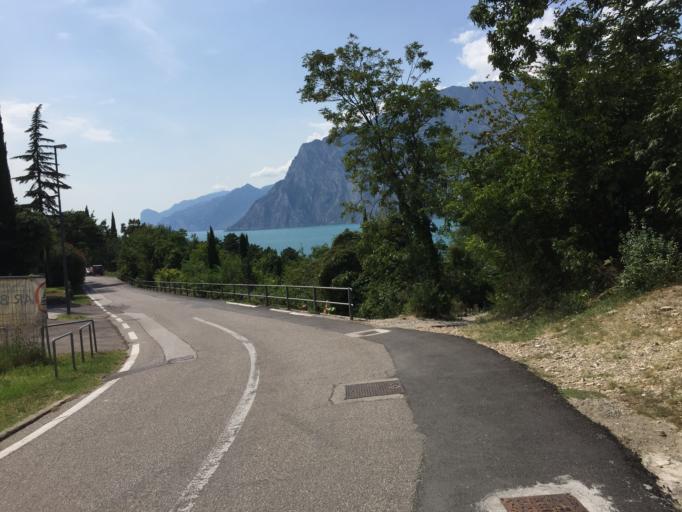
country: IT
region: Trentino-Alto Adige
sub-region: Provincia di Trento
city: Torbole sul Garda
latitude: 45.8668
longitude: 10.8791
